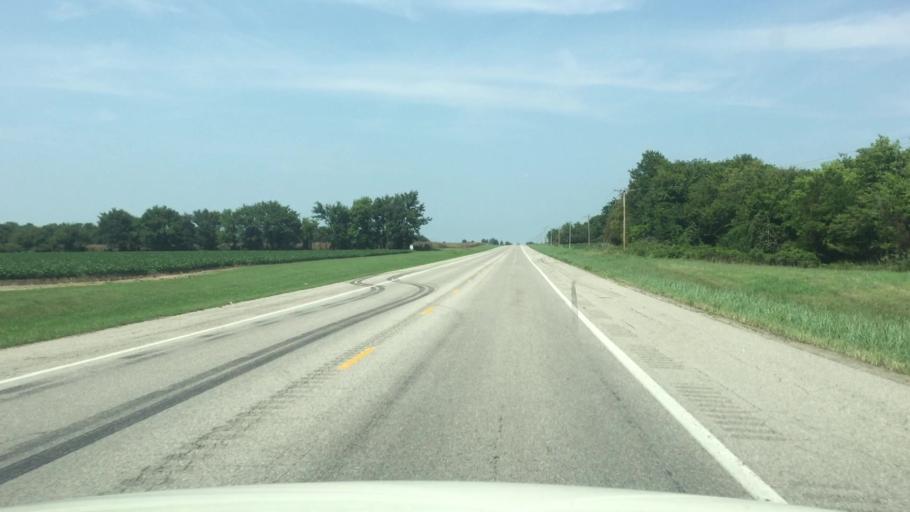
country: US
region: Kansas
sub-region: Crawford County
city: Pittsburg
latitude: 37.2567
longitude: -94.7052
